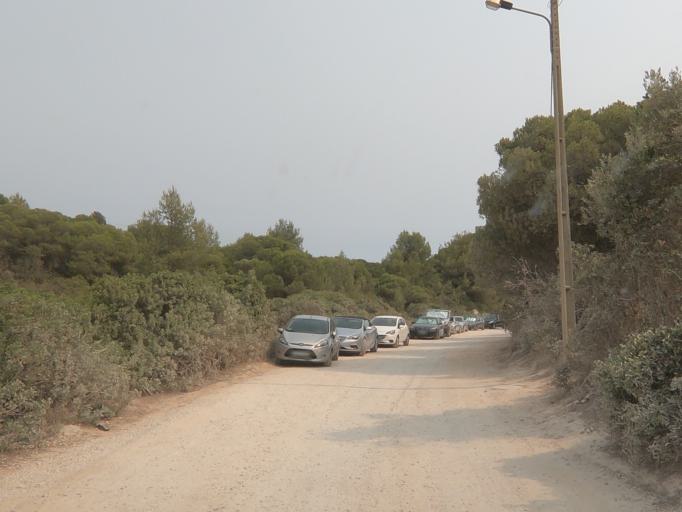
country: PT
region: Faro
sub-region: Silves
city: Armacao de Pera
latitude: 37.0927
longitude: -8.4004
